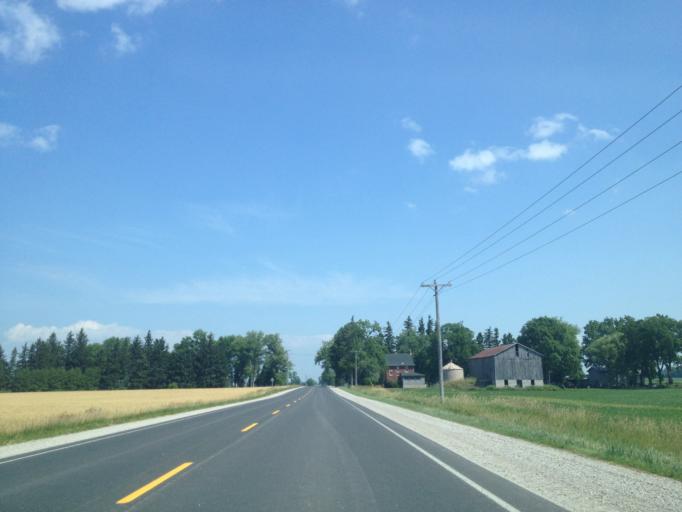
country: CA
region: Ontario
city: Stratford
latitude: 43.3184
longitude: -81.2026
